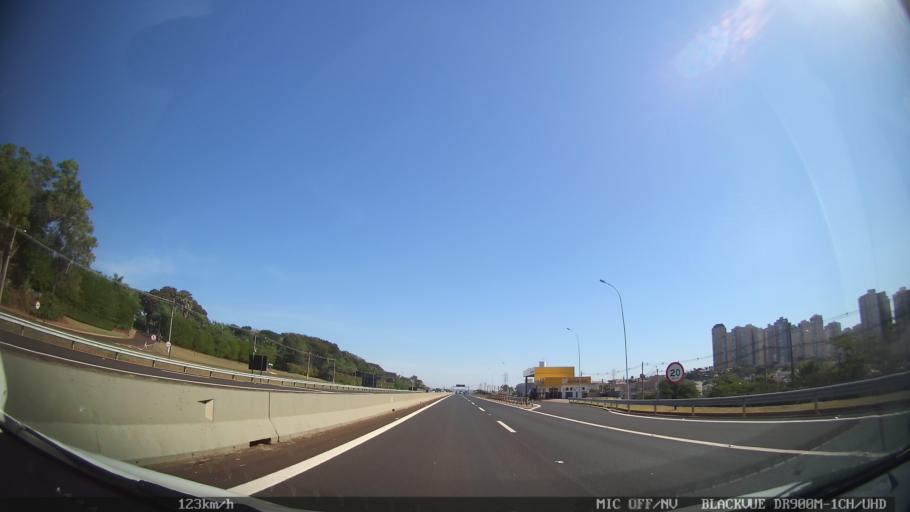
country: BR
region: Sao Paulo
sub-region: Ribeirao Preto
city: Ribeirao Preto
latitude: -21.2229
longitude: -47.7965
